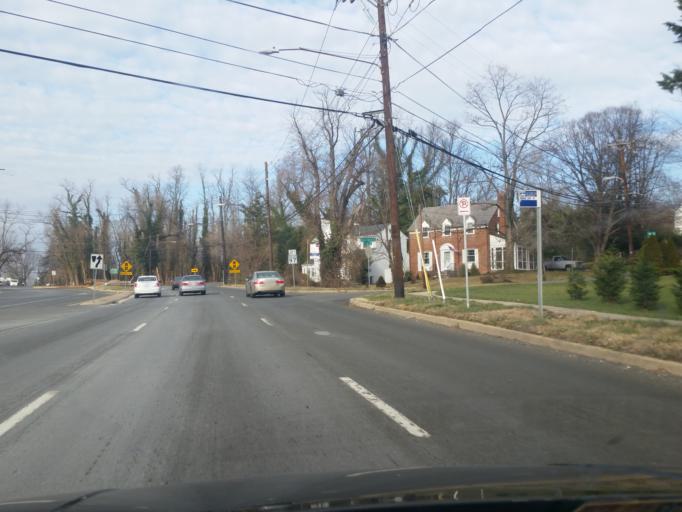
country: US
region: Maryland
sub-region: Montgomery County
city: Forest Glen
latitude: 39.0044
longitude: -77.0400
